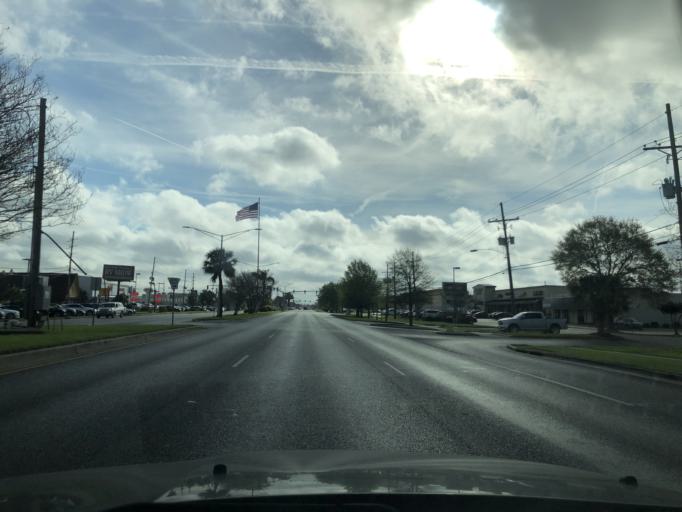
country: US
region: Louisiana
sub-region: Jefferson Parish
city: Kenner
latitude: 30.0060
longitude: -90.2320
